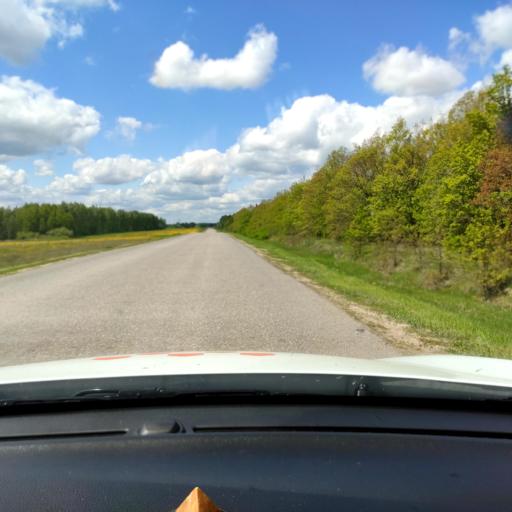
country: RU
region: Tatarstan
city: Kuybyshevskiy Zaton
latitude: 55.3426
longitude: 49.0663
